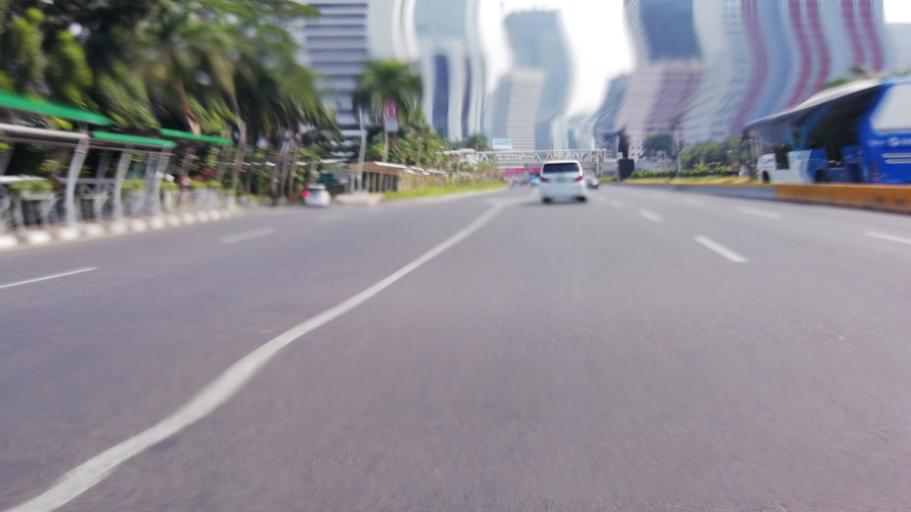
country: ID
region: Jakarta Raya
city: Jakarta
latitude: -6.2031
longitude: 106.8228
